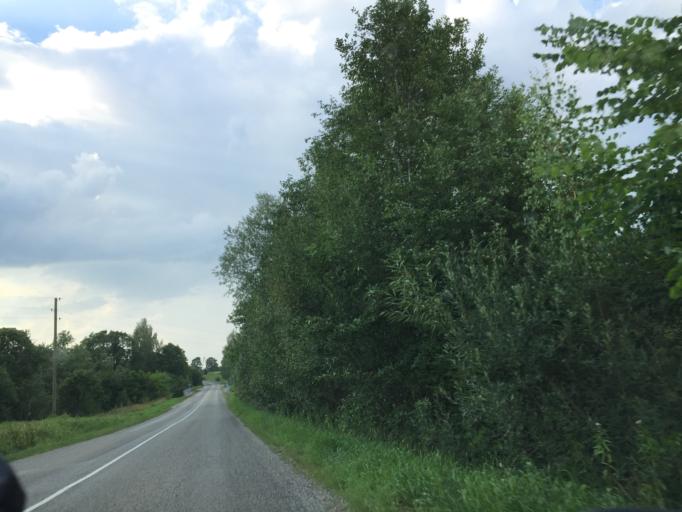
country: LV
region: Dobeles Rajons
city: Dobele
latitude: 56.5994
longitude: 23.3076
